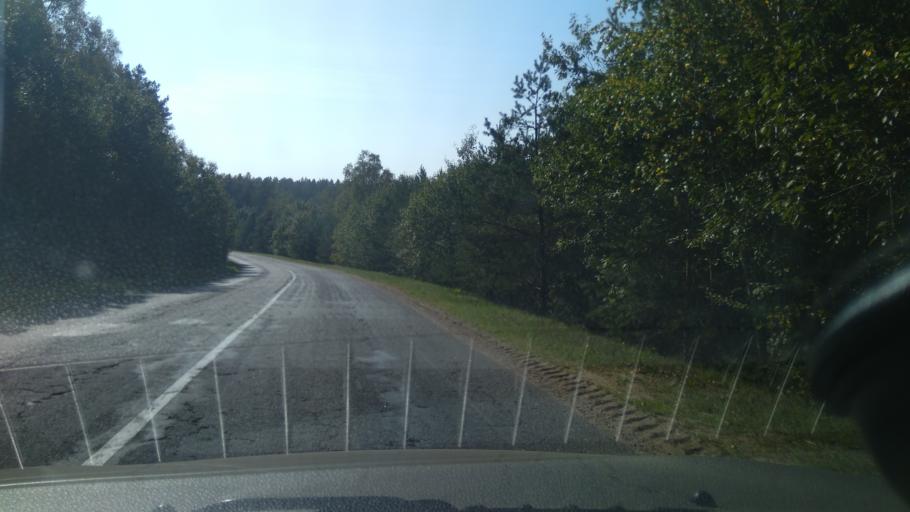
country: BY
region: Minsk
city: Rakaw
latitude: 54.0019
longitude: 27.0452
